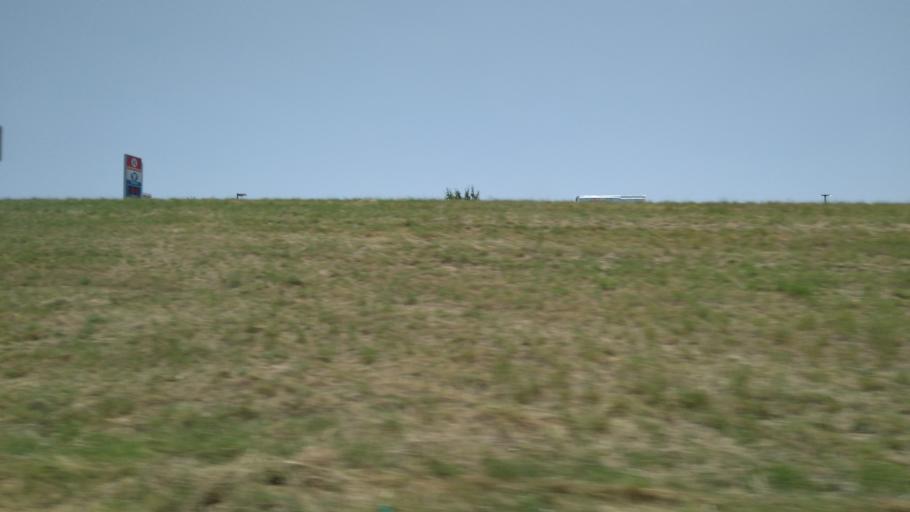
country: US
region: Texas
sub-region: McLennan County
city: Woodway
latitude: 31.5116
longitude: -97.1902
